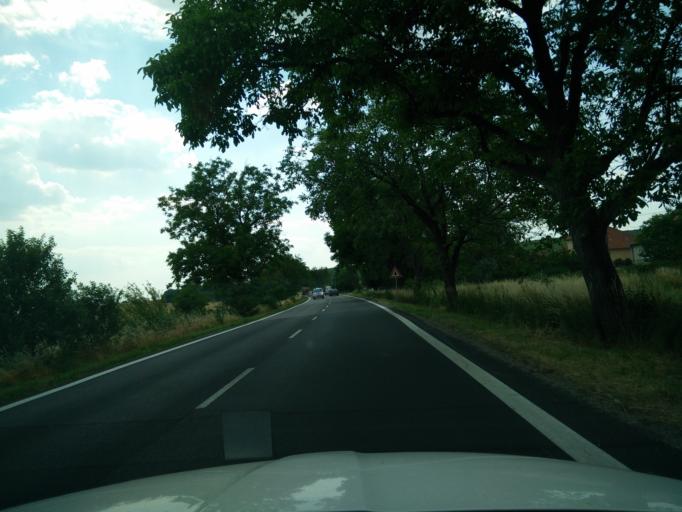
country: SK
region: Nitriansky
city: Partizanske
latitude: 48.6311
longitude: 18.3264
